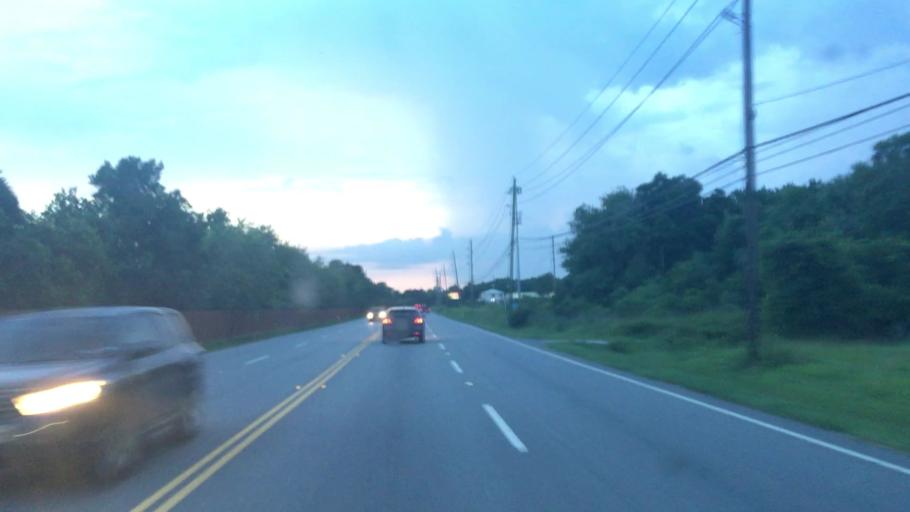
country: US
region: Texas
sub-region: Harris County
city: Humble
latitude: 29.9661
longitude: -95.2394
